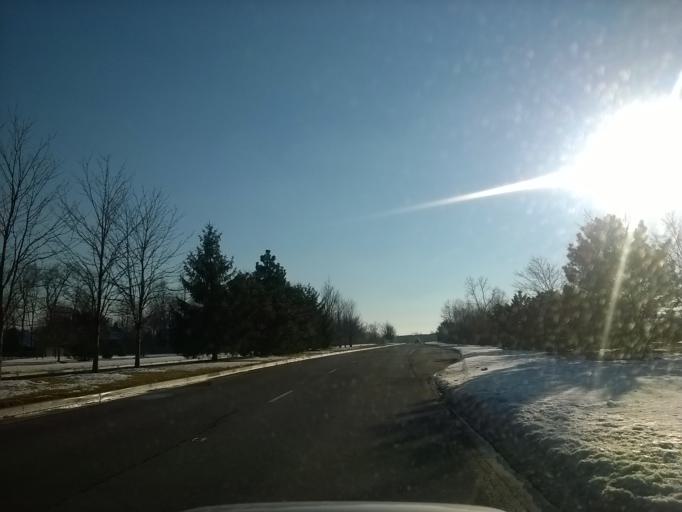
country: US
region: Indiana
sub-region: Hamilton County
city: Carmel
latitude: 39.9653
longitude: -86.0714
